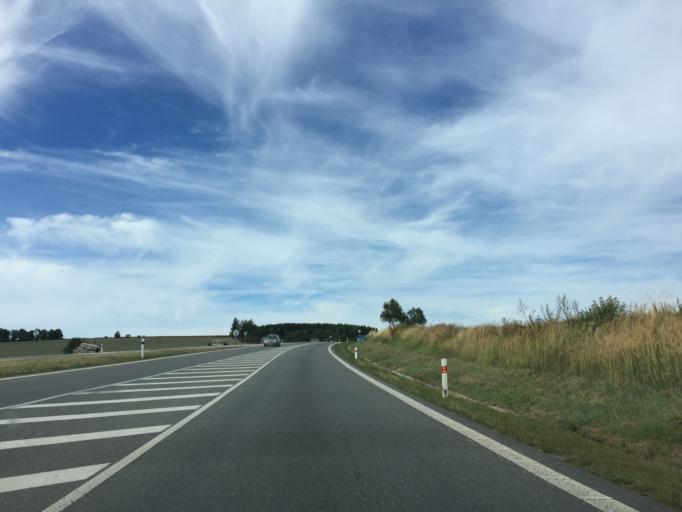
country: CZ
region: Jihocesky
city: Chotoviny
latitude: 49.5463
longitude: 14.6646
